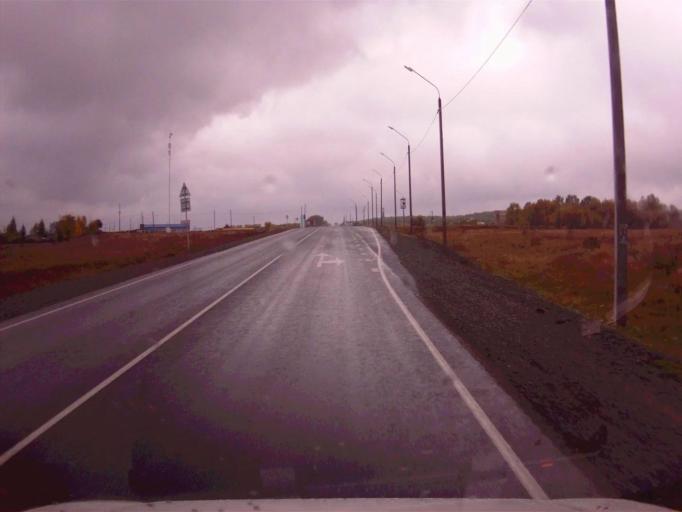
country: RU
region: Chelyabinsk
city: Tayginka
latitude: 55.4976
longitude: 60.6421
